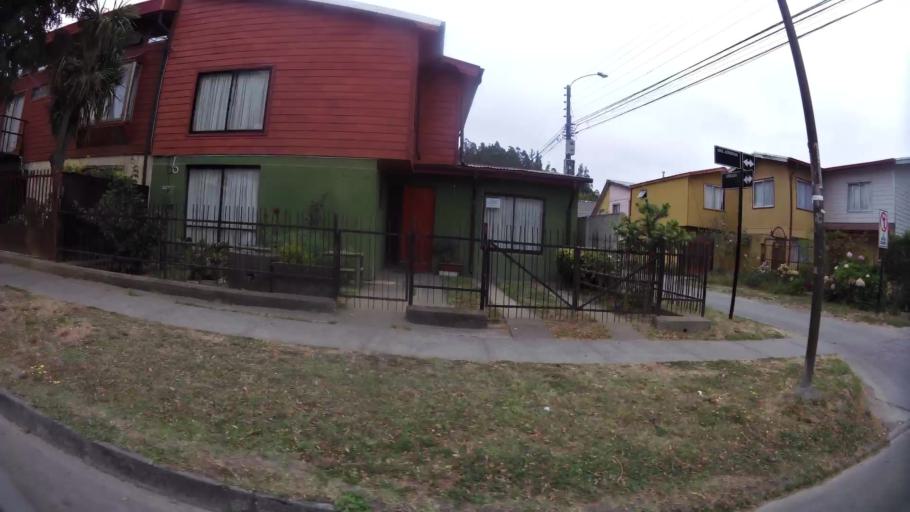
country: CL
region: Biobio
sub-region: Provincia de Concepcion
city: Concepcion
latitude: -36.8243
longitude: -73.0168
